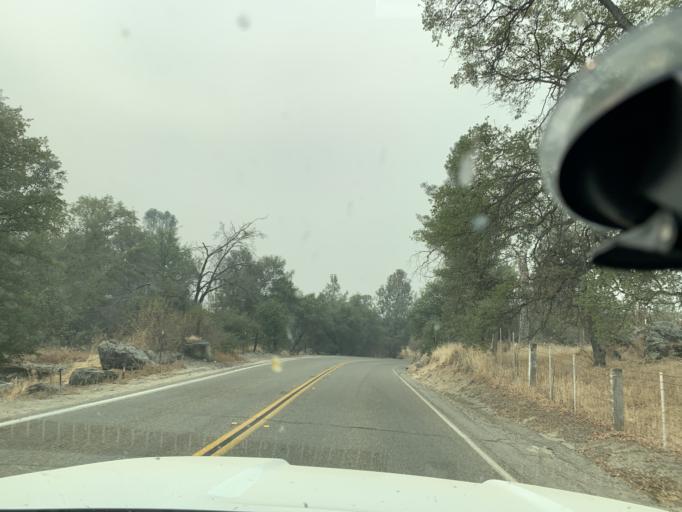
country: US
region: California
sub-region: Fresno County
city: Auberry
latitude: 37.0511
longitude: -119.4979
